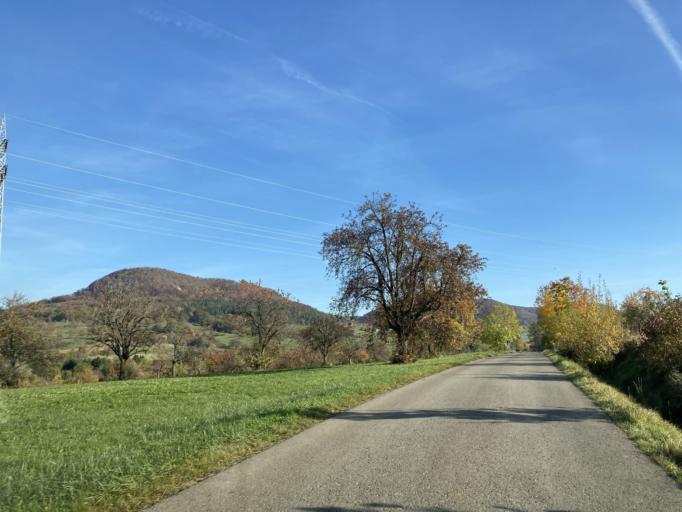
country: DE
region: Baden-Wuerttemberg
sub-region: Tuebingen Region
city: Mossingen
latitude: 48.4004
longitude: 9.0827
